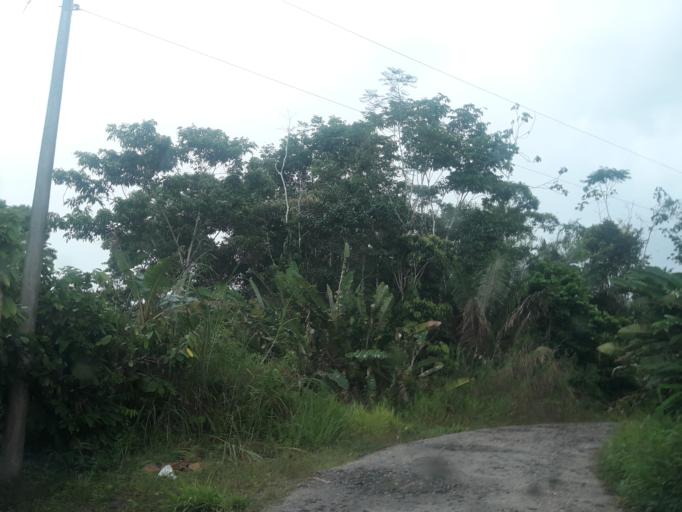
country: EC
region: Napo
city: Tena
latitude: -1.1013
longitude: -77.6879
